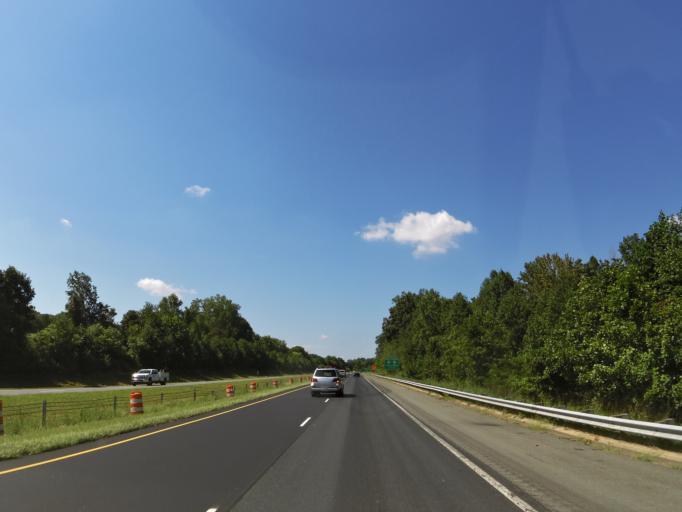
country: US
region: North Carolina
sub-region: Lincoln County
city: Lincolnton
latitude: 35.4504
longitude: -81.2161
